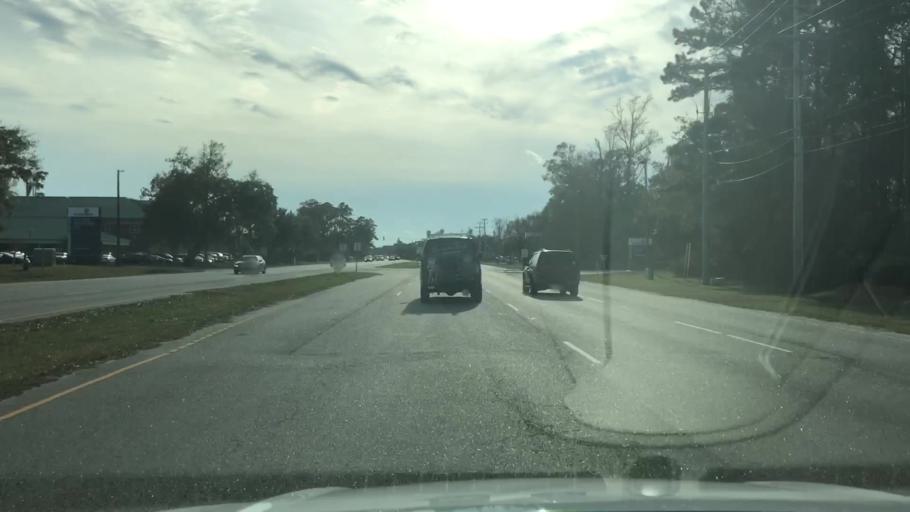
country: US
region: South Carolina
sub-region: Georgetown County
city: Murrells Inlet
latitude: 33.5607
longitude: -79.0404
